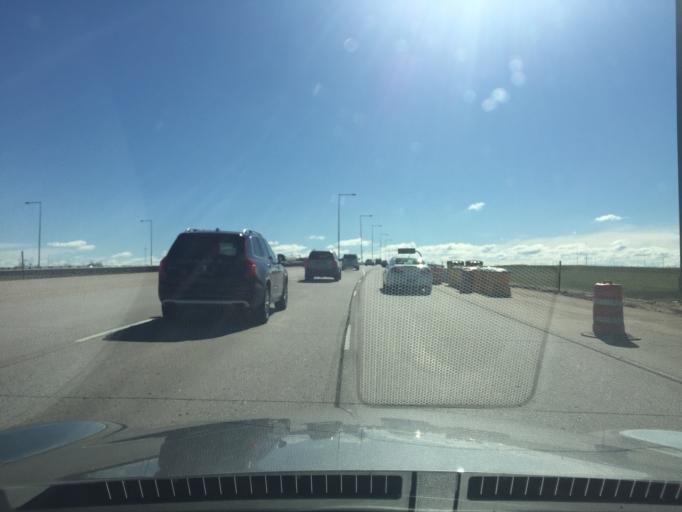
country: US
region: Colorado
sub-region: Adams County
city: Aurora
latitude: 39.8336
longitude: -104.7174
